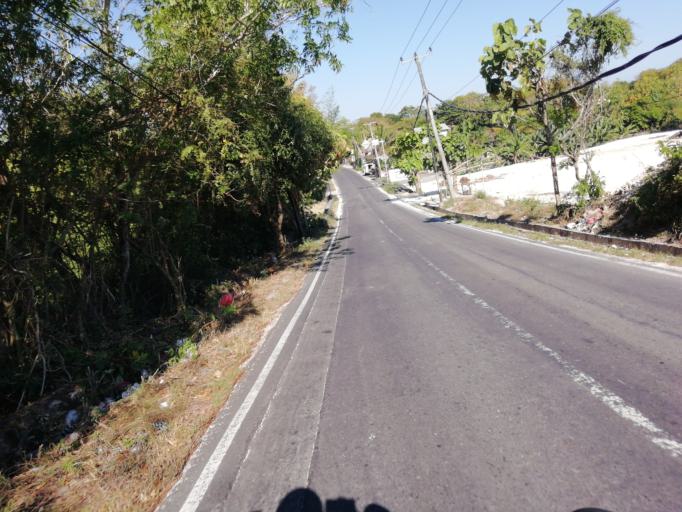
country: ID
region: Bali
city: Jimbaran
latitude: -8.8287
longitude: 115.1725
